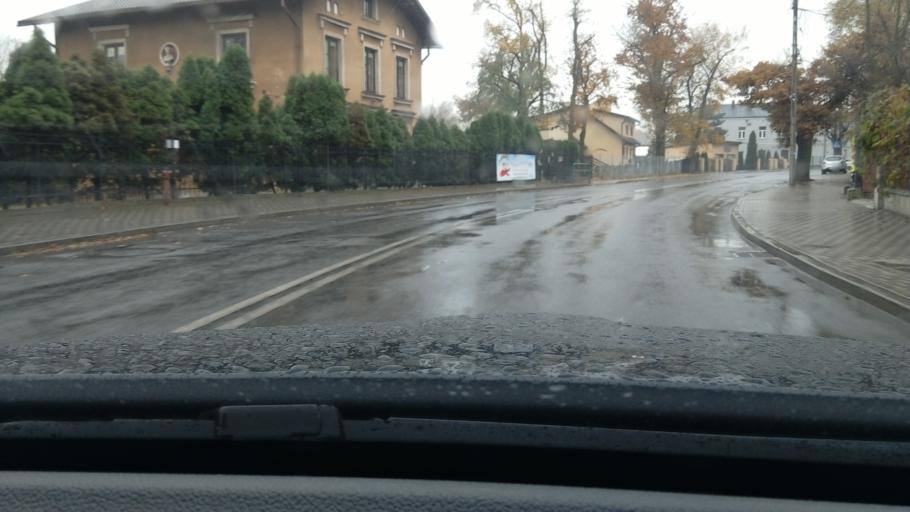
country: PL
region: Lodz Voivodeship
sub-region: Skierniewice
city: Skierniewice
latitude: 51.9586
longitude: 20.1382
